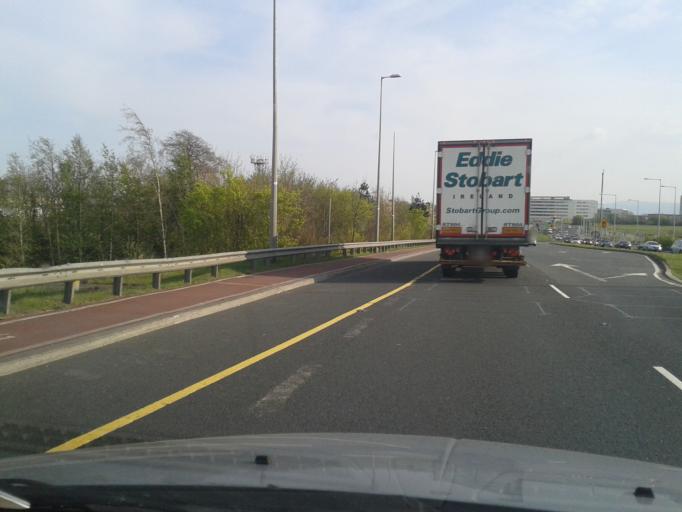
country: IE
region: Leinster
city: Ballymun
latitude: 53.4069
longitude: -6.2653
